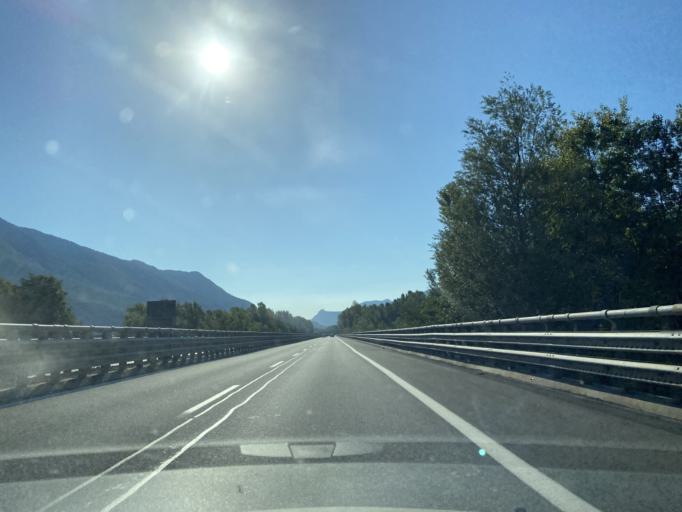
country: IT
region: Piedmont
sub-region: Provincia di Torino
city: San Giorio
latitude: 45.1323
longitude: 7.1824
